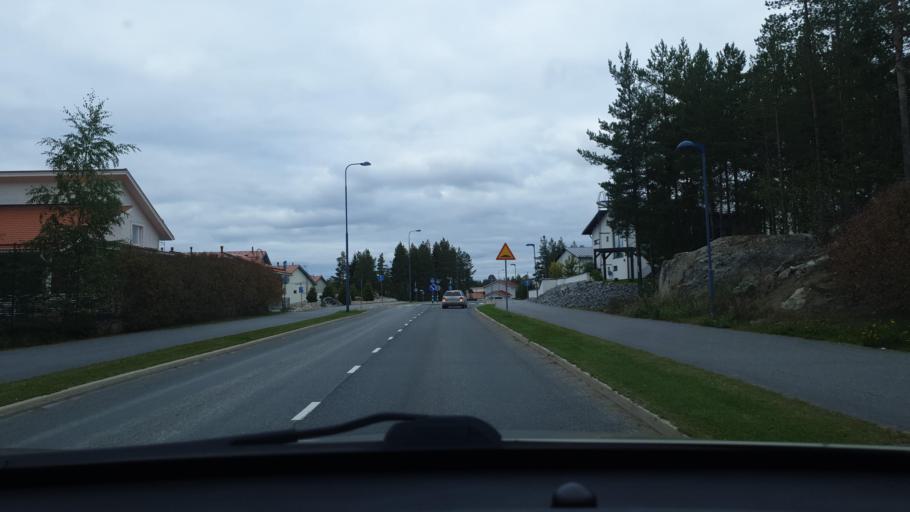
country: FI
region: Ostrobothnia
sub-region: Vaasa
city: Korsholm
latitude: 63.1205
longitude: 21.6570
